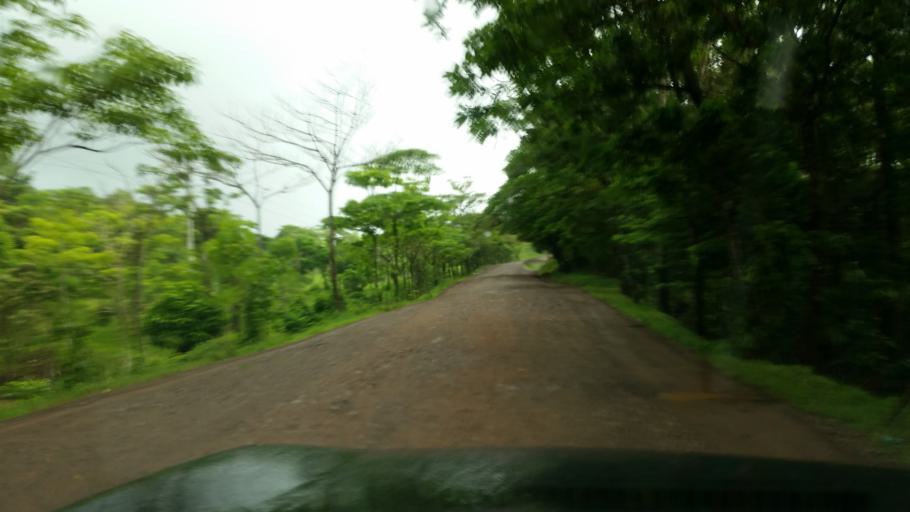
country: NI
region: Atlantico Norte (RAAN)
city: Siuna
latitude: 13.4035
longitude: -84.8539
